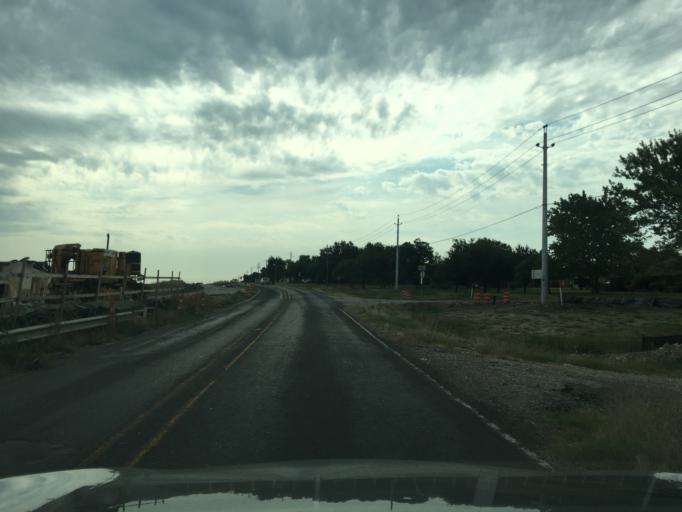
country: US
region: Texas
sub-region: Collin County
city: Saint Paul
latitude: 33.0547
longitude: -96.5756
